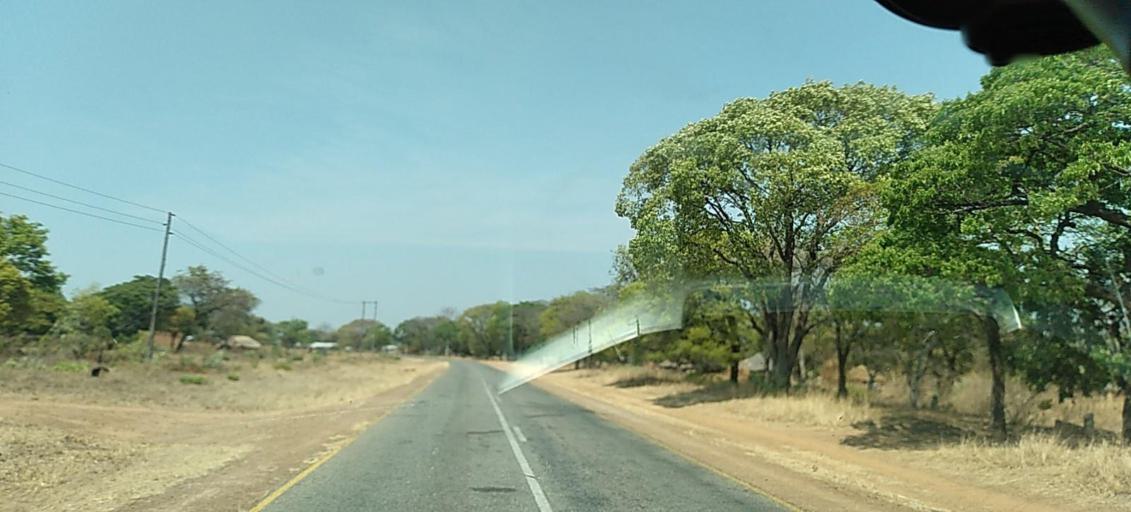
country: ZM
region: North-Western
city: Kabompo
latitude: -13.3760
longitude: 24.3806
